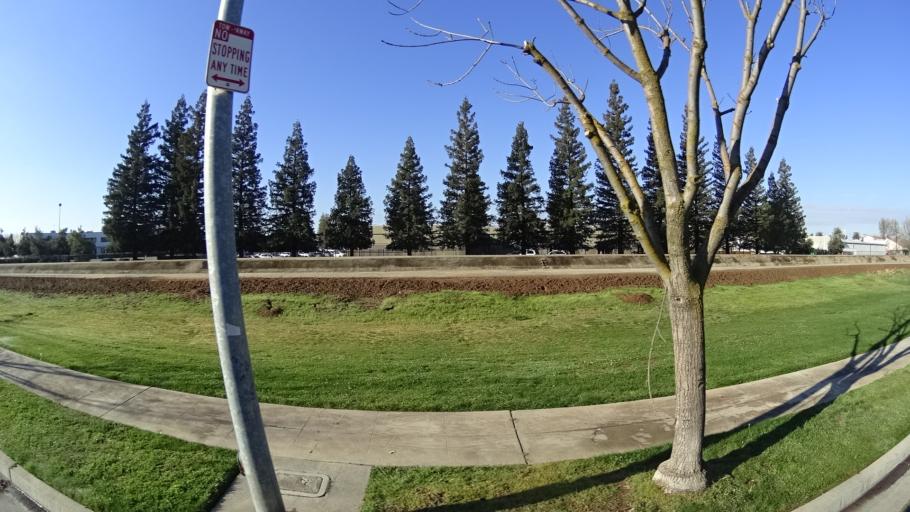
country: US
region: California
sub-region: Fresno County
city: West Park
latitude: 36.8122
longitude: -119.8702
